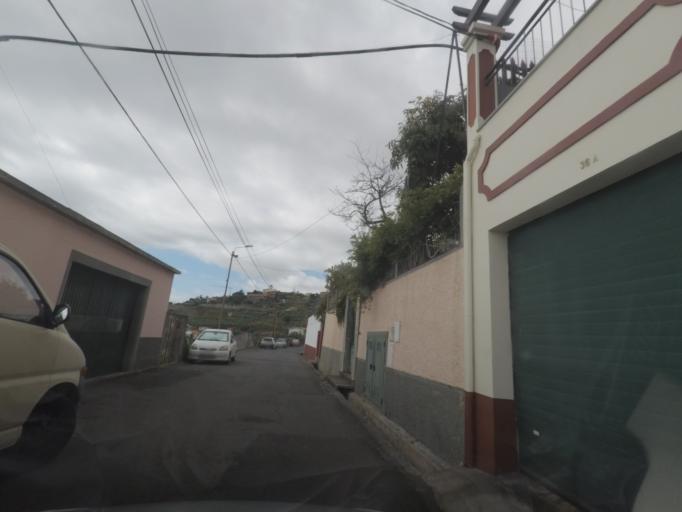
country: PT
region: Madeira
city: Camara de Lobos
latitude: 32.6469
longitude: -16.9449
